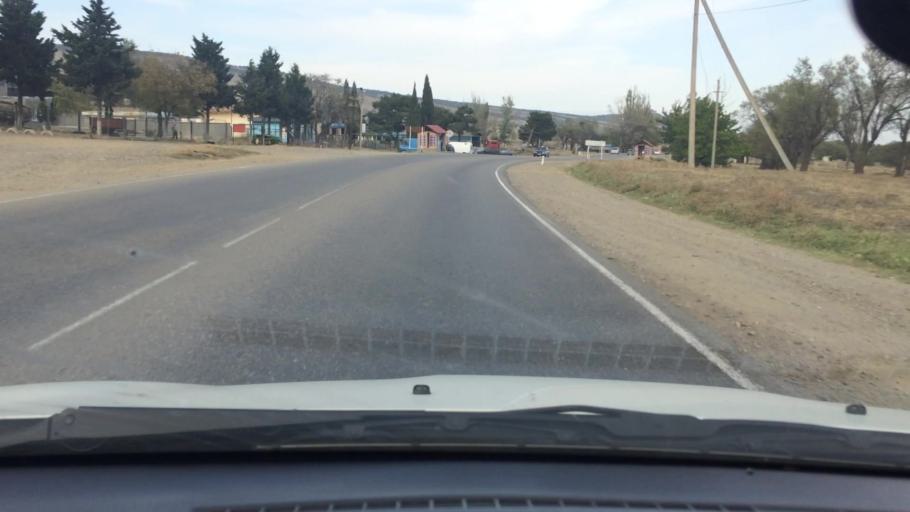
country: GE
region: T'bilisi
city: Tbilisi
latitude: 41.6287
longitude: 44.8081
